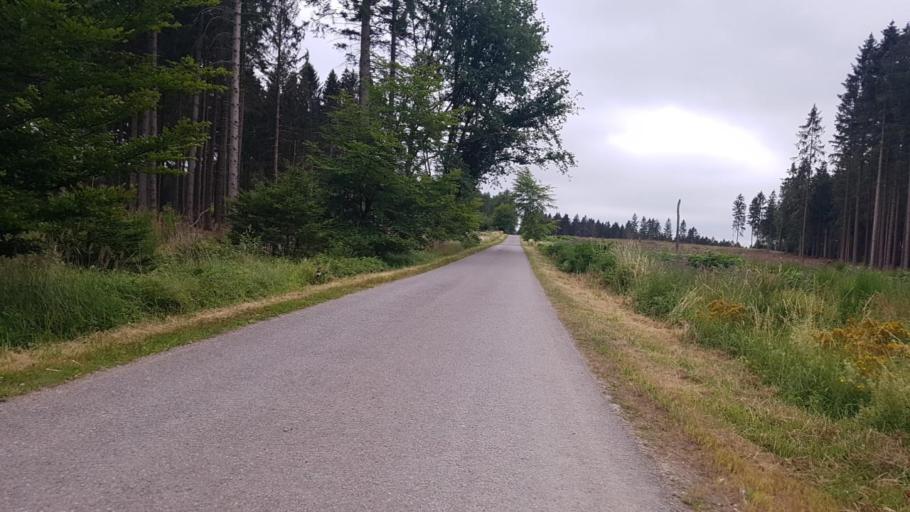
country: DE
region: North Rhine-Westphalia
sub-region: Regierungsbezirk Koln
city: Hurtgenwald
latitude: 50.7566
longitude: 6.3843
